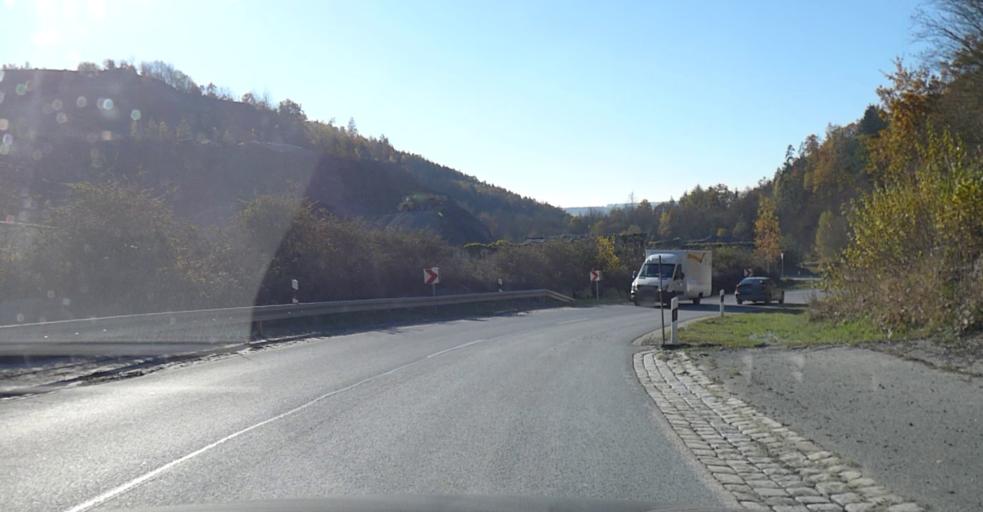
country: DE
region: Bavaria
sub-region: Upper Franconia
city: Kupferberg
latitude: 50.1347
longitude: 11.5675
